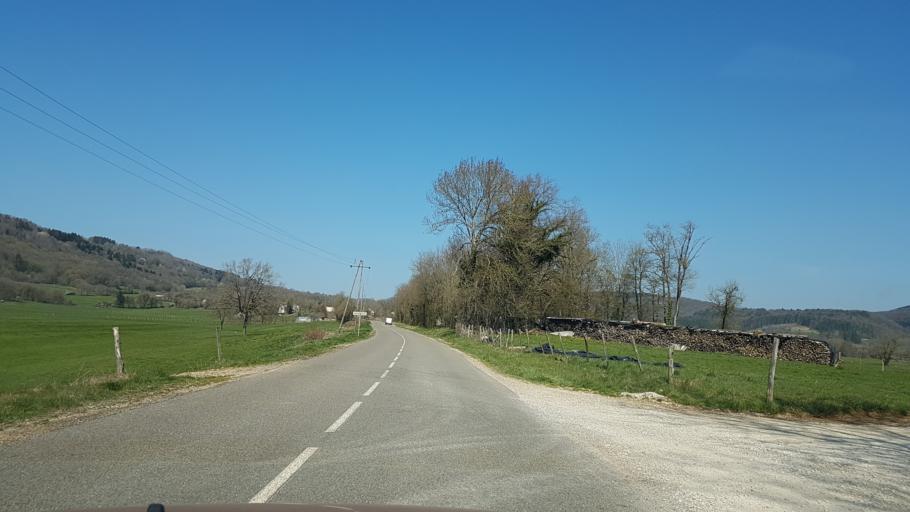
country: FR
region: Bourgogne
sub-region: Departement de Saone-et-Loire
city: Cuiseaux
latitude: 46.4711
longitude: 5.4521
